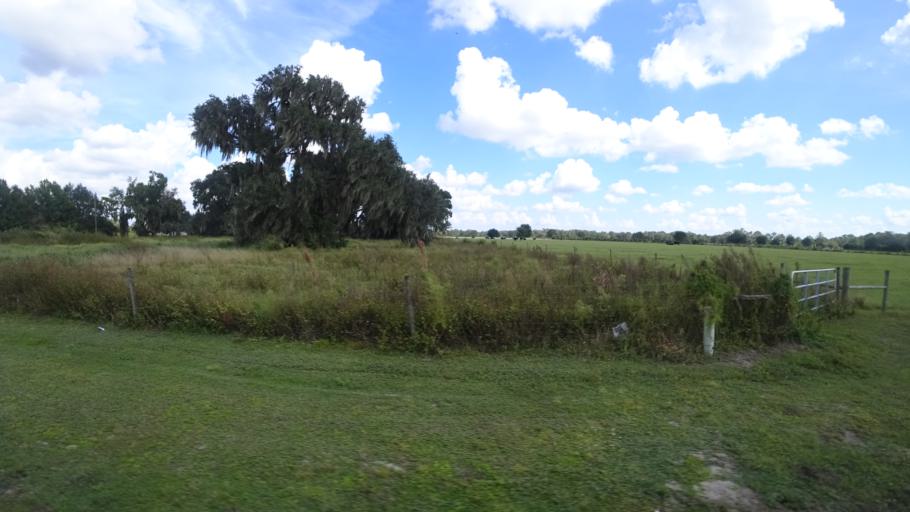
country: US
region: Florida
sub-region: Hardee County
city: Wauchula
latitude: 27.4831
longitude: -82.0797
